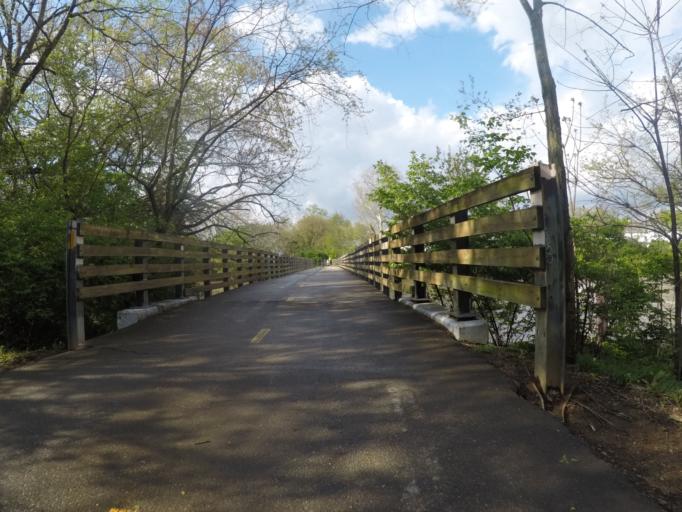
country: US
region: Ohio
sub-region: Franklin County
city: Grandview Heights
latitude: 40.0217
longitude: -83.0199
